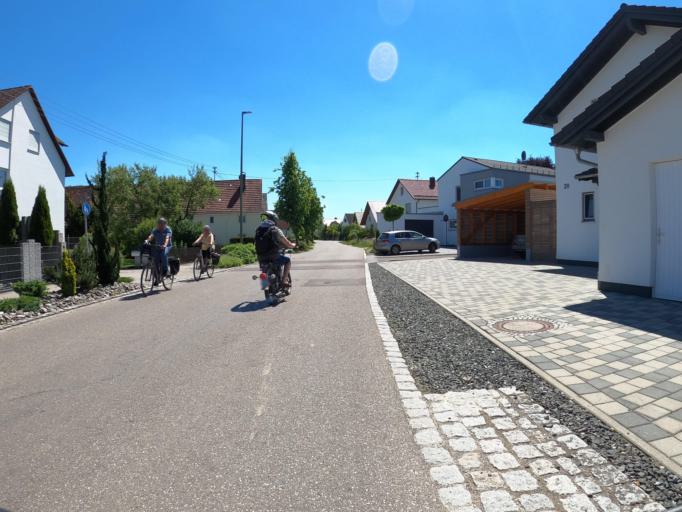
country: DE
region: Bavaria
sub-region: Swabia
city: Pfaffenhofen an der Roth
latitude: 48.3492
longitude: 10.1542
